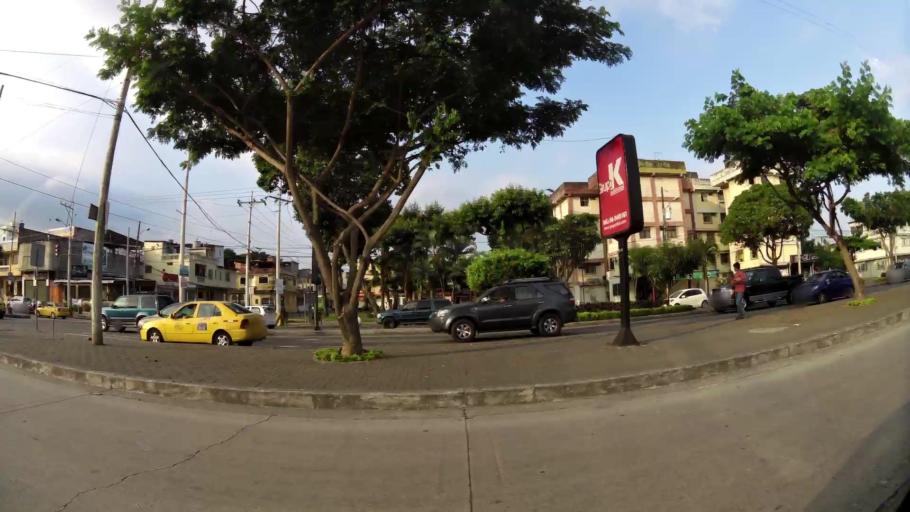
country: EC
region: Guayas
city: Eloy Alfaro
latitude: -2.1361
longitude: -79.8935
